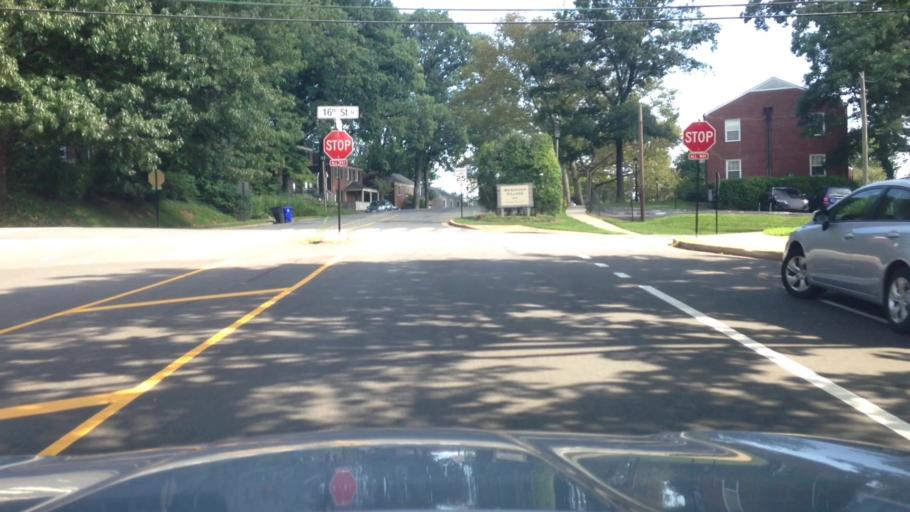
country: US
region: Virginia
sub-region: Fairfax County
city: Seven Corners
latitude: 38.8861
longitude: -77.1377
